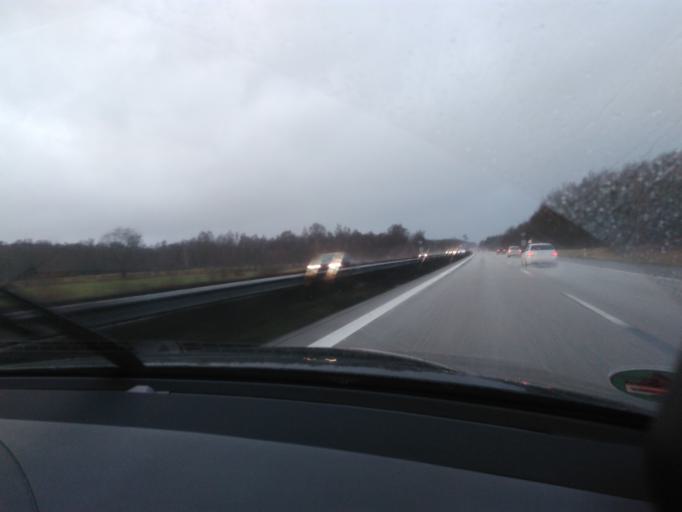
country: DE
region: Schleswig-Holstein
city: Schmalfeld
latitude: 53.8848
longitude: 9.9447
